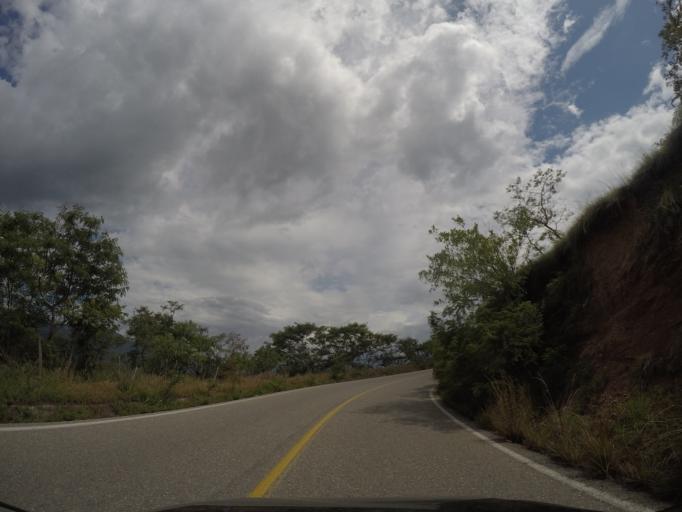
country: MX
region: Oaxaca
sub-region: San Jeronimo Coatlan
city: San Cristobal Honduras
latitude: 16.4304
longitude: -97.0677
